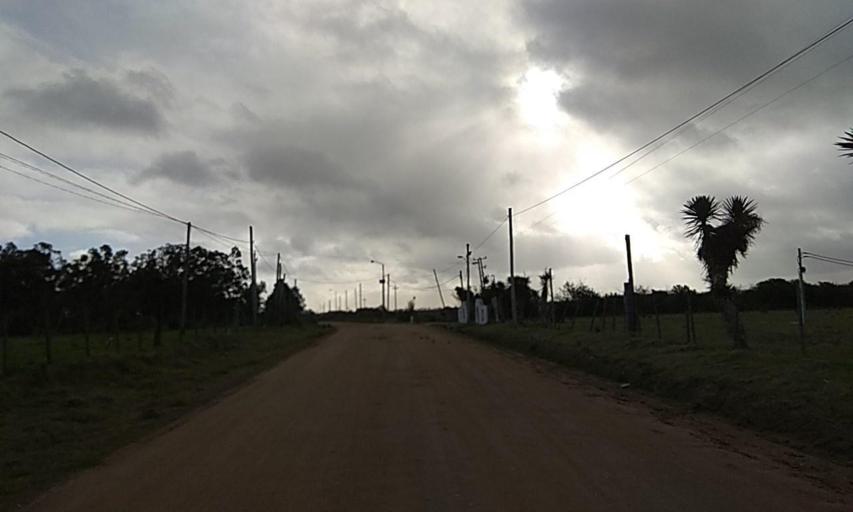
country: UY
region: Florida
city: Florida
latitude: -34.0748
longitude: -56.1984
